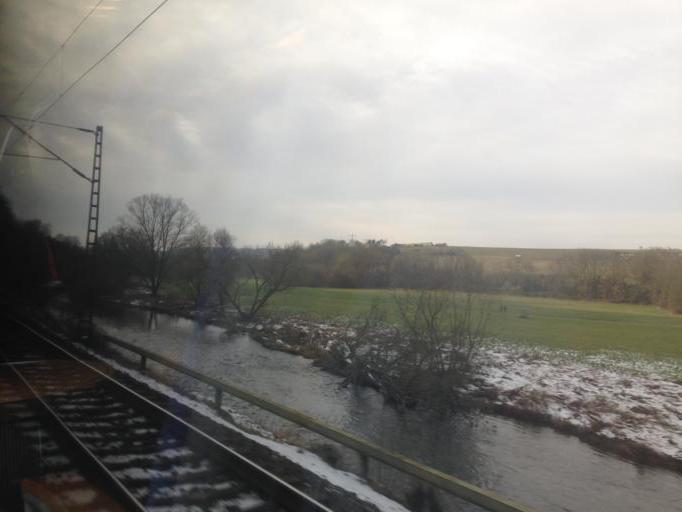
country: DE
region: Hesse
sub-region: Regierungsbezirk Giessen
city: Asslar
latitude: 50.5903
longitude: 8.4461
